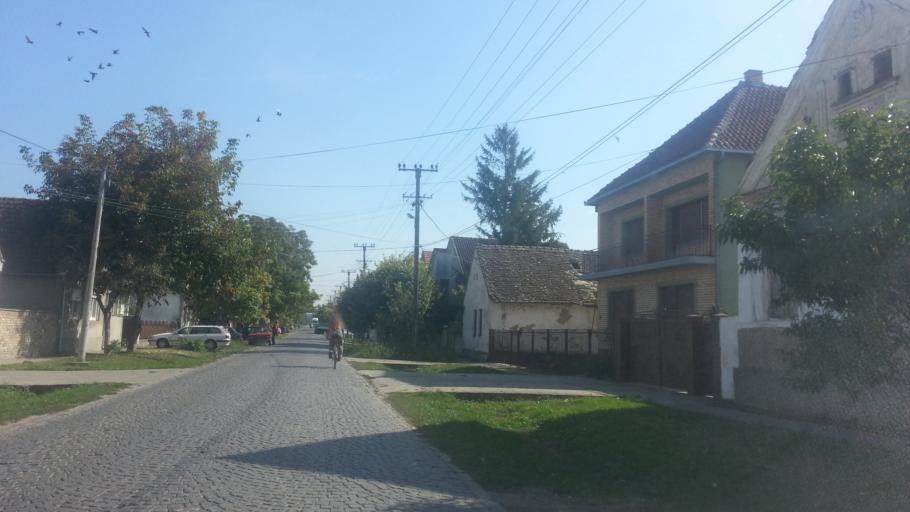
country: RS
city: Stari Banovci
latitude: 44.9936
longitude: 20.2852
